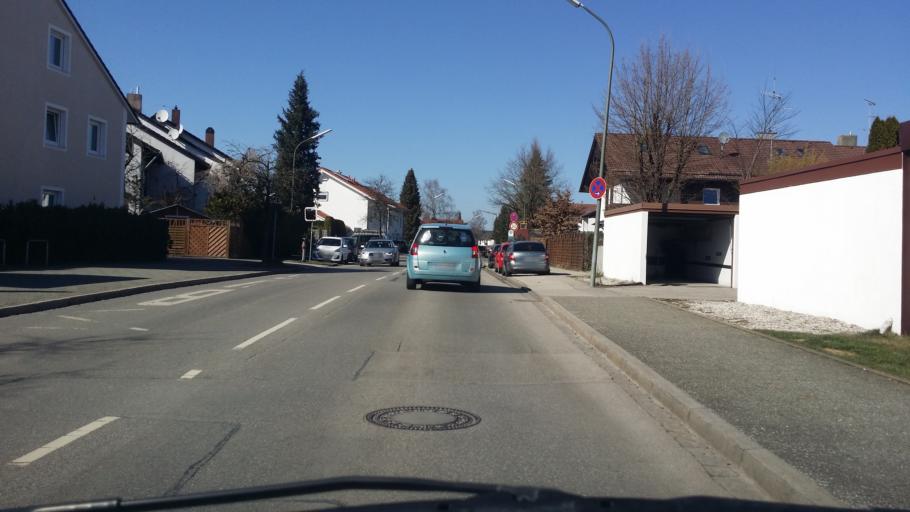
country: DE
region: Bavaria
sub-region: Upper Bavaria
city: Geretsried
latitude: 47.8731
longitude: 11.4711
